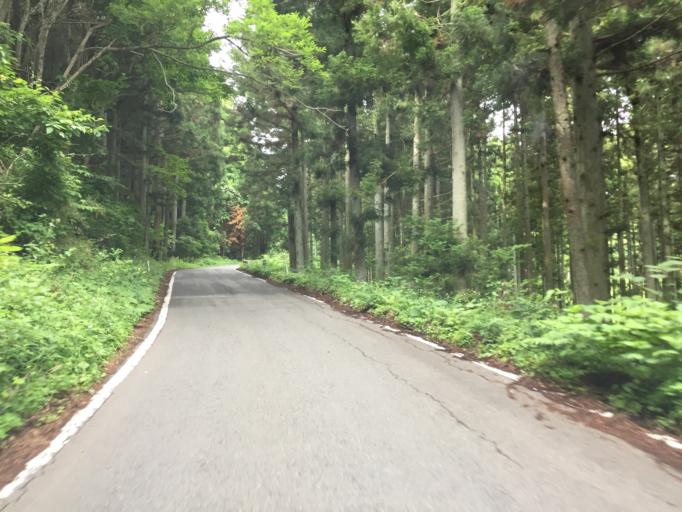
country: JP
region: Fukushima
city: Funehikimachi-funehiki
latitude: 37.4664
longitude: 140.6392
